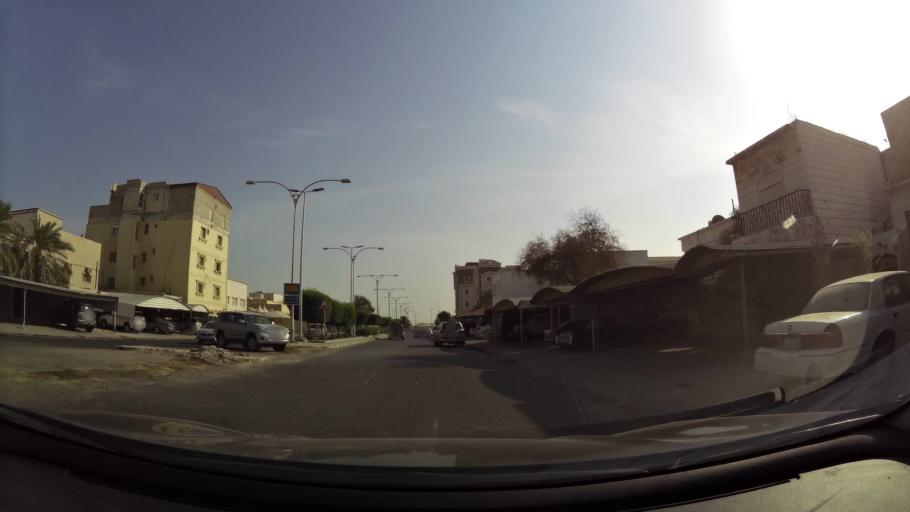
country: KW
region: Al Ahmadi
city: Ar Riqqah
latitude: 29.1383
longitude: 48.1085
